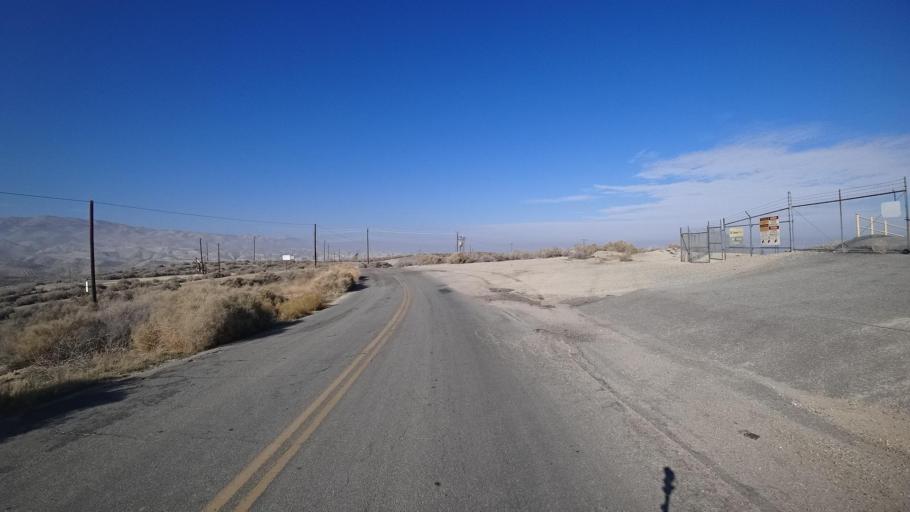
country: US
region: California
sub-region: Kern County
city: Taft Heights
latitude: 35.1158
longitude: -119.4767
